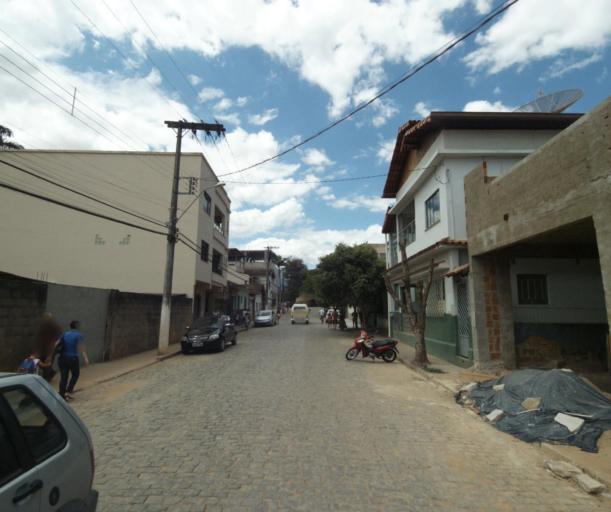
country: BR
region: Espirito Santo
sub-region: Mimoso Do Sul
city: Mimoso do Sul
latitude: -21.0635
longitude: -41.3687
